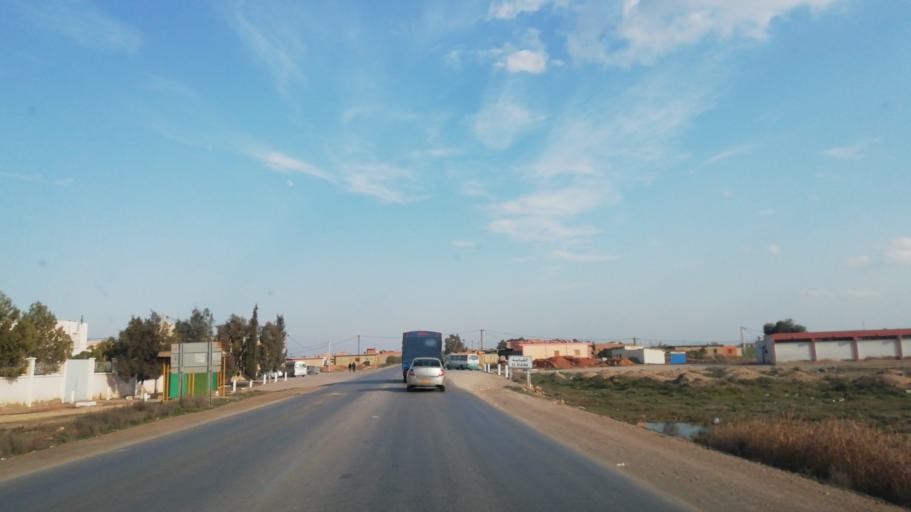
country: DZ
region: Relizane
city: Relizane
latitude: 35.8980
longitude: 0.5858
